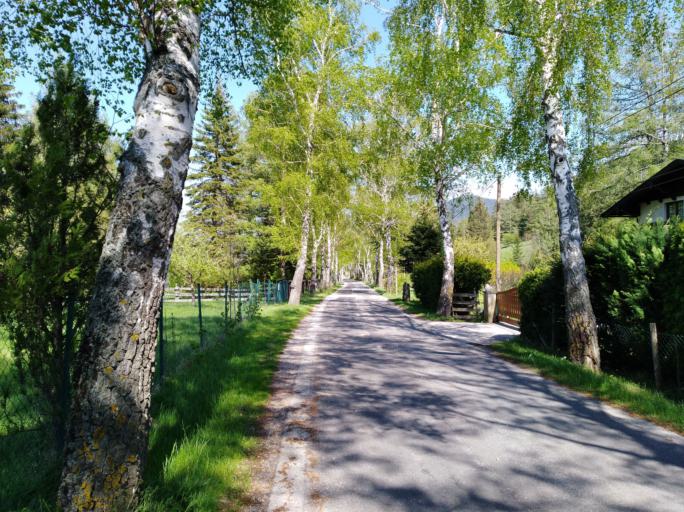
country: AT
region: Lower Austria
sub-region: Politischer Bezirk Neunkirchen
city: Puchberg am Schneeberg
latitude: 47.7830
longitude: 15.8881
